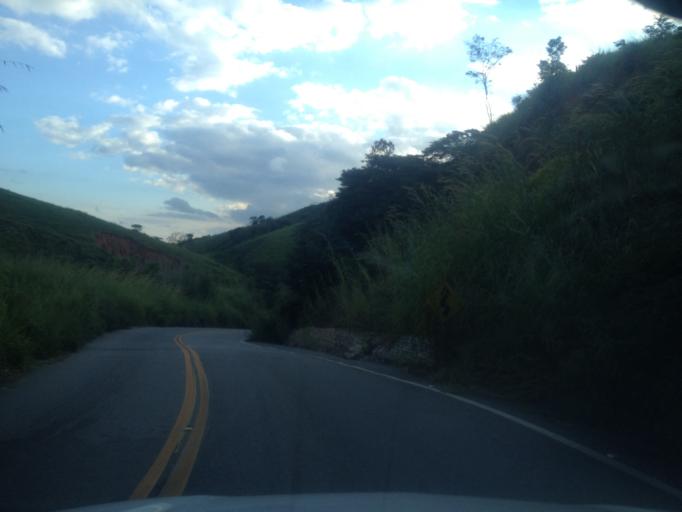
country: BR
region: Rio de Janeiro
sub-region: Quatis
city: Quatis
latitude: -22.3828
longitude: -44.2626
